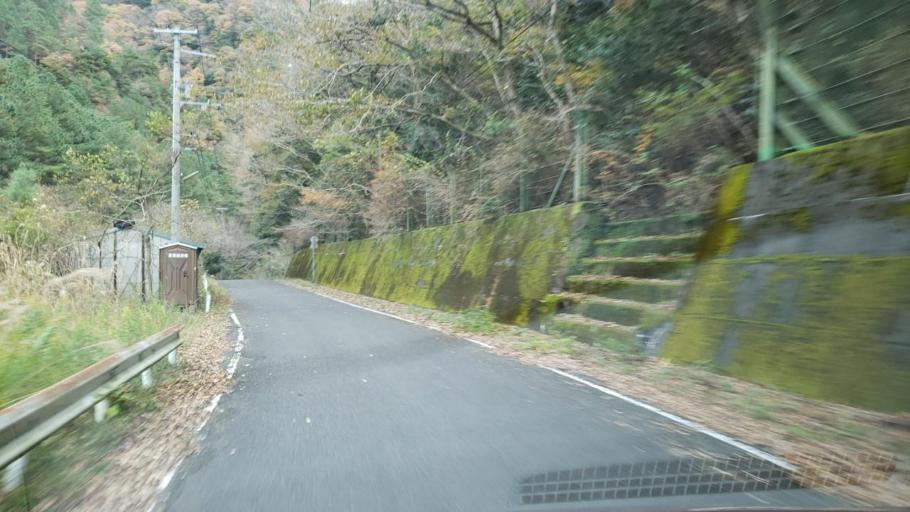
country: JP
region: Tokushima
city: Wakimachi
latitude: 34.1355
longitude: 134.2296
